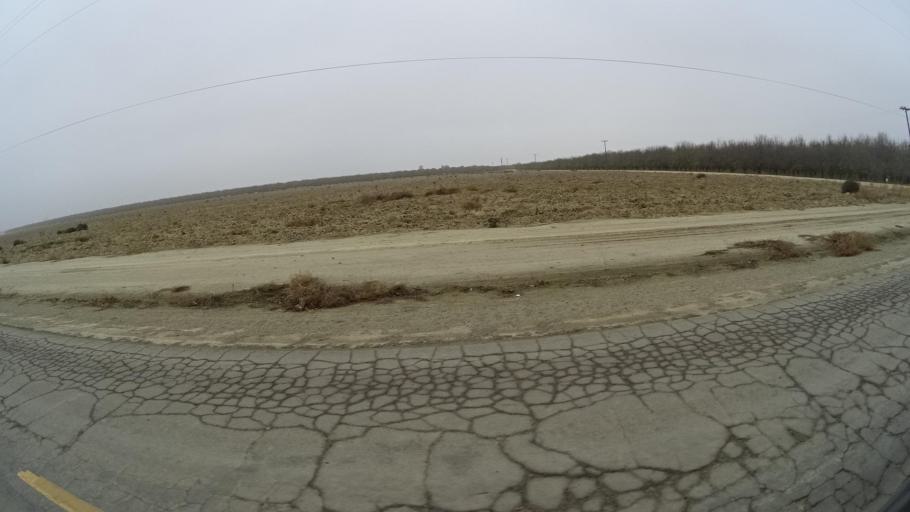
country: US
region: California
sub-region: Kern County
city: Wasco
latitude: 35.6224
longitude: -119.5090
